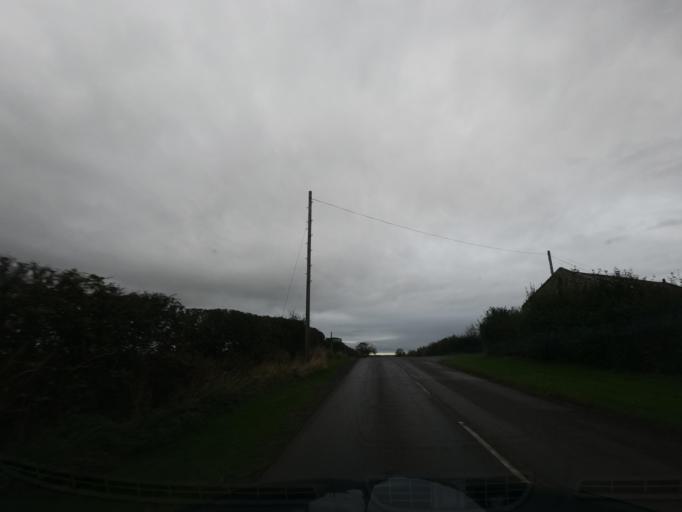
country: GB
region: England
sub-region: Northumberland
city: Ancroft
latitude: 55.7039
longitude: -2.0610
